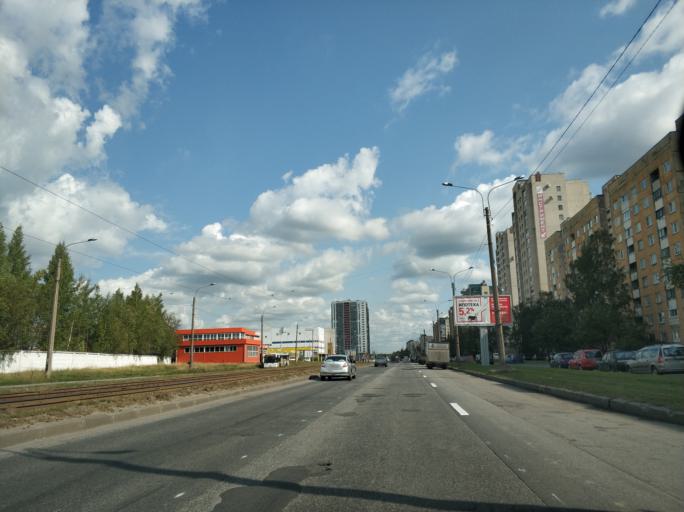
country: RU
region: St.-Petersburg
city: Krasnogvargeisky
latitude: 59.9567
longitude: 30.4705
